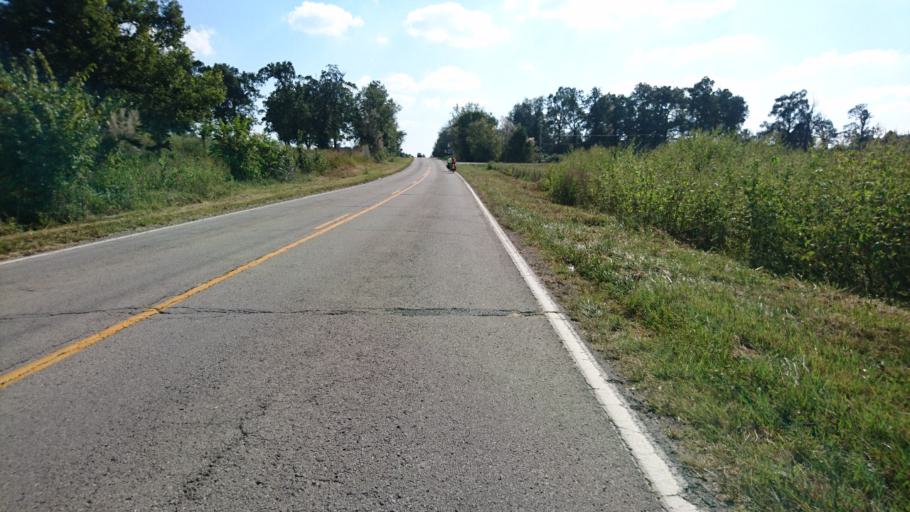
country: US
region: Missouri
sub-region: Laclede County
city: Lebanon
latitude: 37.6274
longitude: -92.6896
